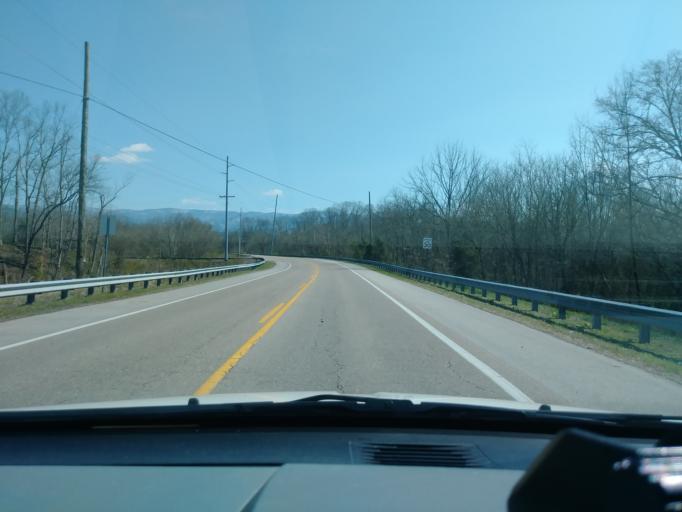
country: US
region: Tennessee
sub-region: Greene County
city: Tusculum
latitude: 36.1194
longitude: -82.7840
